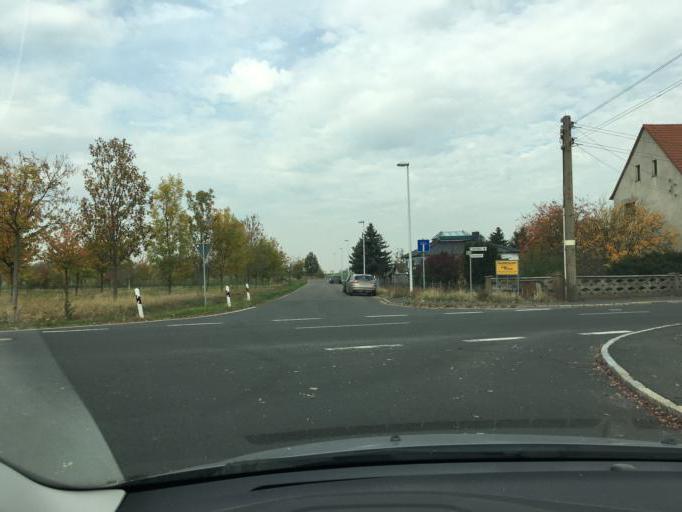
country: DE
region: Saxony
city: Zwochau
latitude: 51.4238
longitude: 12.2889
